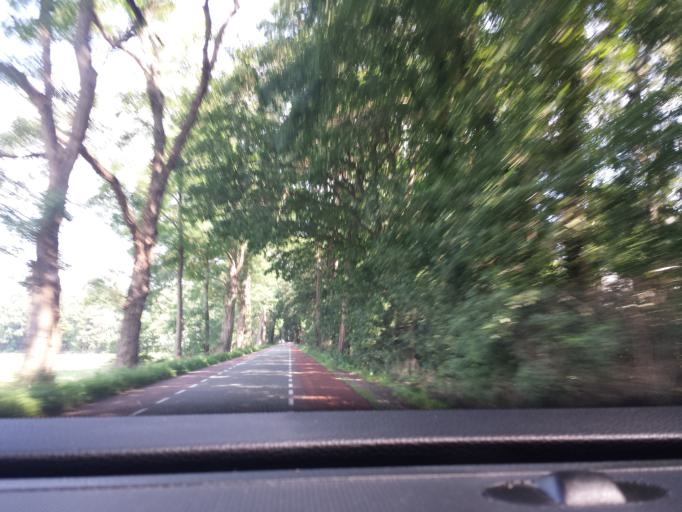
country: NL
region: Gelderland
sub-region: Gemeente Bronckhorst
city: Hengelo
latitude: 52.1065
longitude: 6.3416
